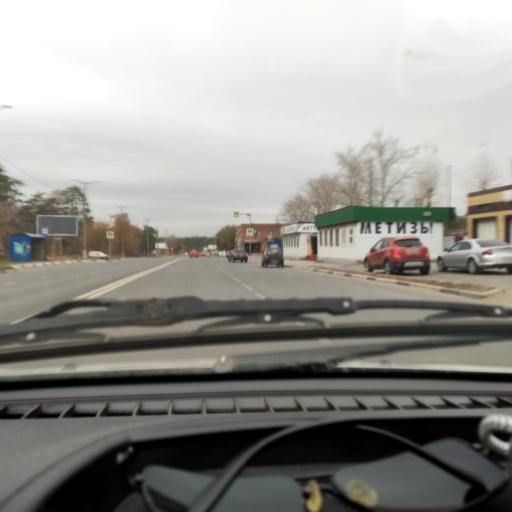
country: RU
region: Samara
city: Zhigulevsk
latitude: 53.4942
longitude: 49.4738
